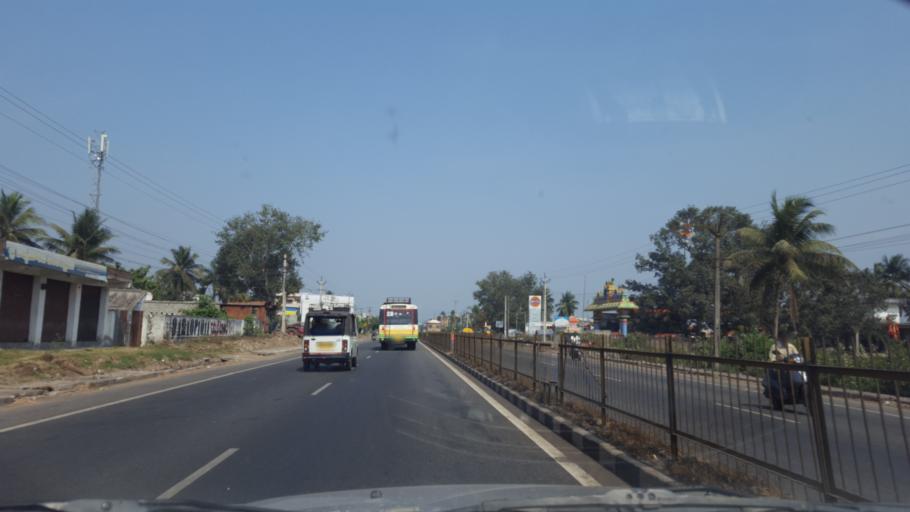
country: IN
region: Andhra Pradesh
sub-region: Vishakhapatnam
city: Anakapalle
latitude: 17.6805
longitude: 82.9806
